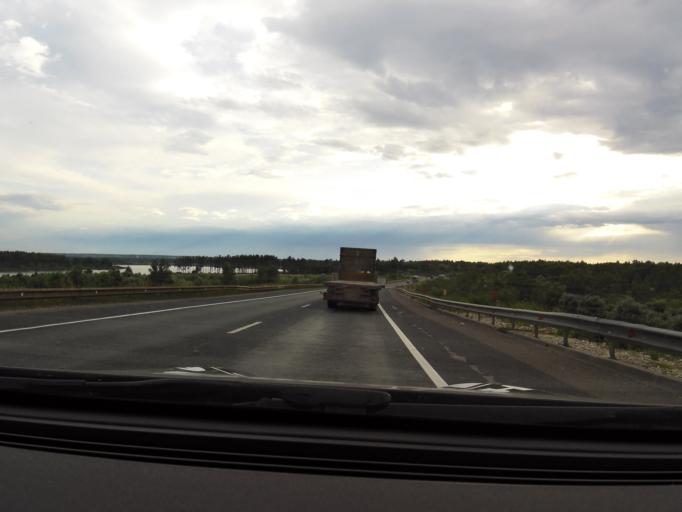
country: RU
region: Vladimir
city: Kommunar
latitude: 56.0539
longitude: 40.4304
